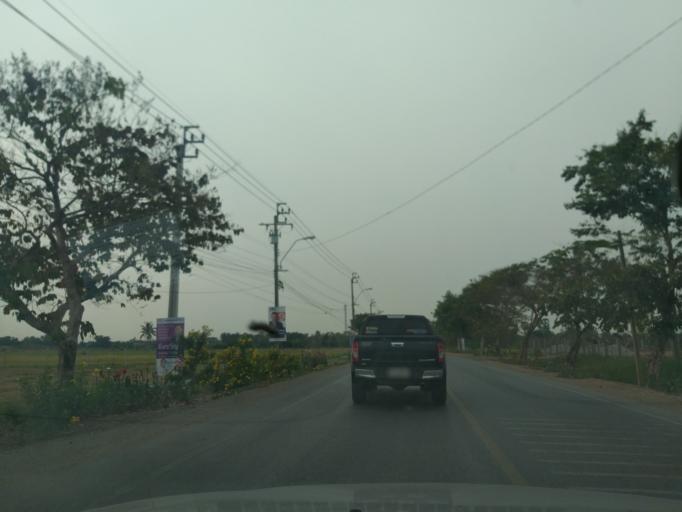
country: TH
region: Bangkok
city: Nong Chok
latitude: 13.8392
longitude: 100.9018
